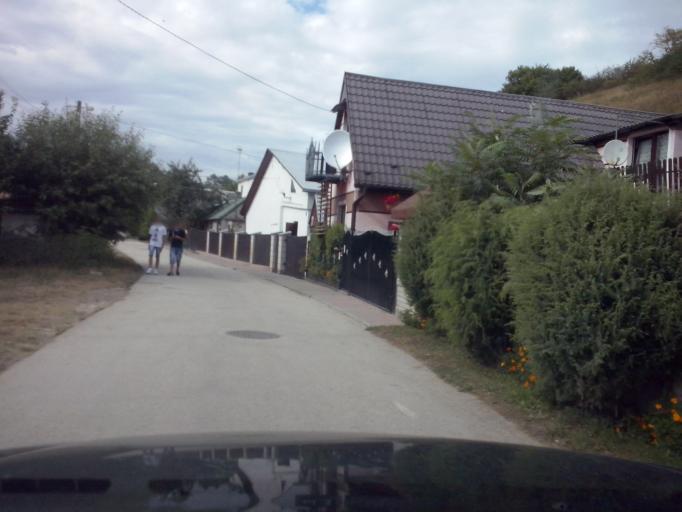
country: PL
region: Swietokrzyskie
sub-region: Powiat kielecki
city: Lagow
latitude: 50.7781
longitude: 21.0884
